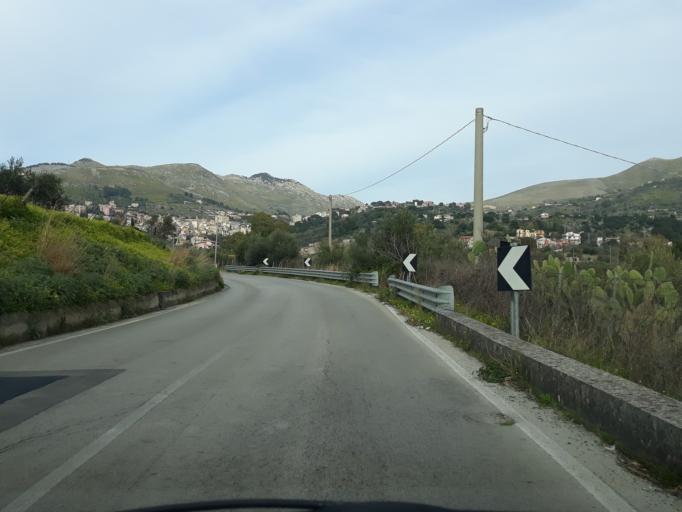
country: IT
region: Sicily
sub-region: Palermo
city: Giardinello
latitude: 38.0783
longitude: 13.1608
